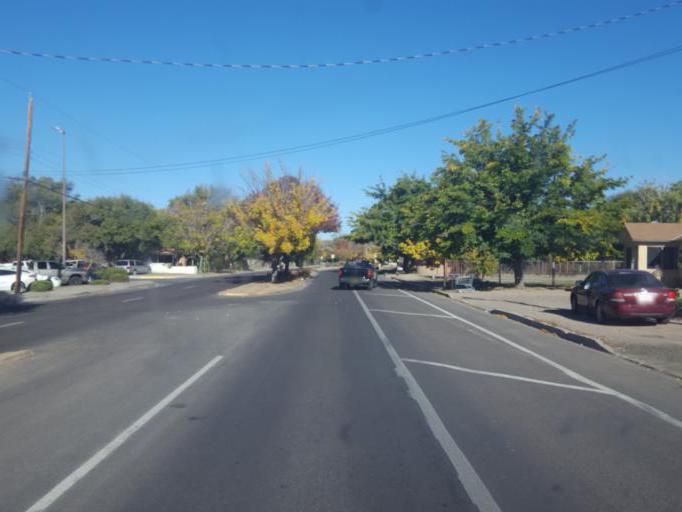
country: US
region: New Mexico
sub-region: Bernalillo County
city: Albuquerque
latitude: 35.0877
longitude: -106.6865
